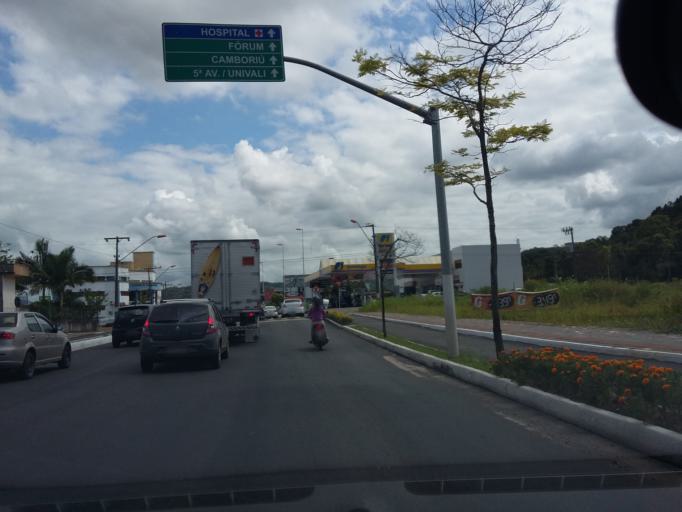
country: BR
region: Santa Catarina
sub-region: Balneario Camboriu
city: Balneario Camboriu
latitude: -26.9933
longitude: -48.6501
